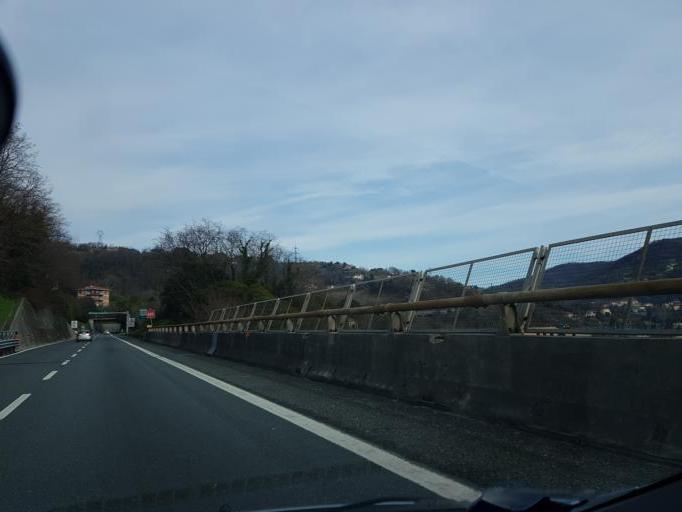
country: IT
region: Liguria
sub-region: Provincia di Genova
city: Manesseno
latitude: 44.4740
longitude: 8.9108
